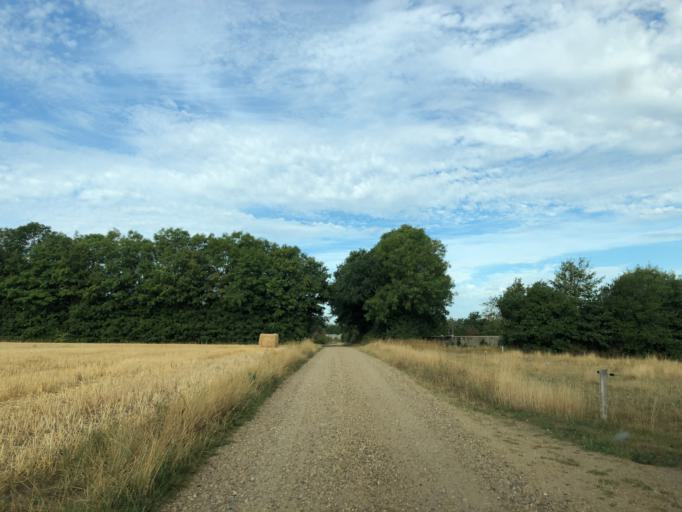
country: DK
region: Central Jutland
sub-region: Ringkobing-Skjern Kommune
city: Skjern
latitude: 56.0406
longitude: 8.4333
